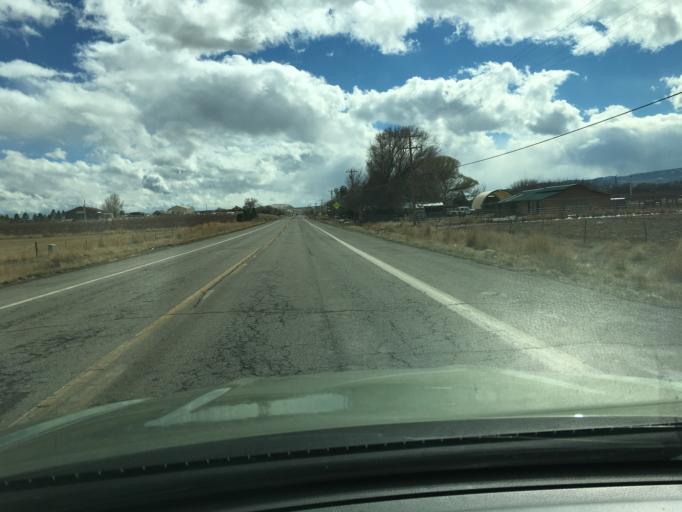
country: US
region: Colorado
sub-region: Mesa County
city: Clifton
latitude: 39.0392
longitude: -108.4595
